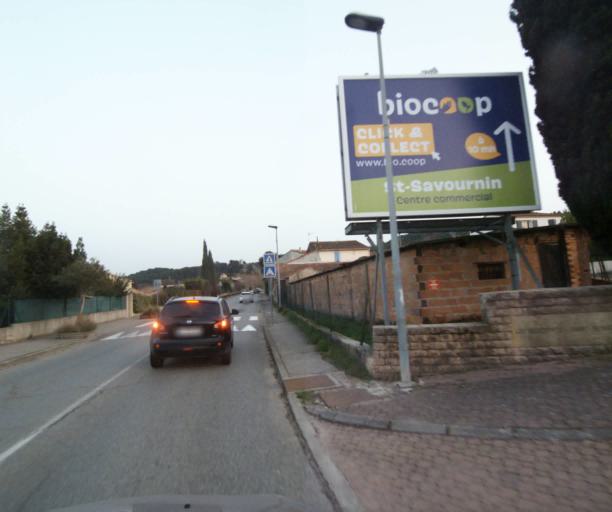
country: FR
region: Provence-Alpes-Cote d'Azur
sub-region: Departement des Bouches-du-Rhone
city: Simiane-Collongue
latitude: 43.4322
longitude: 5.4327
